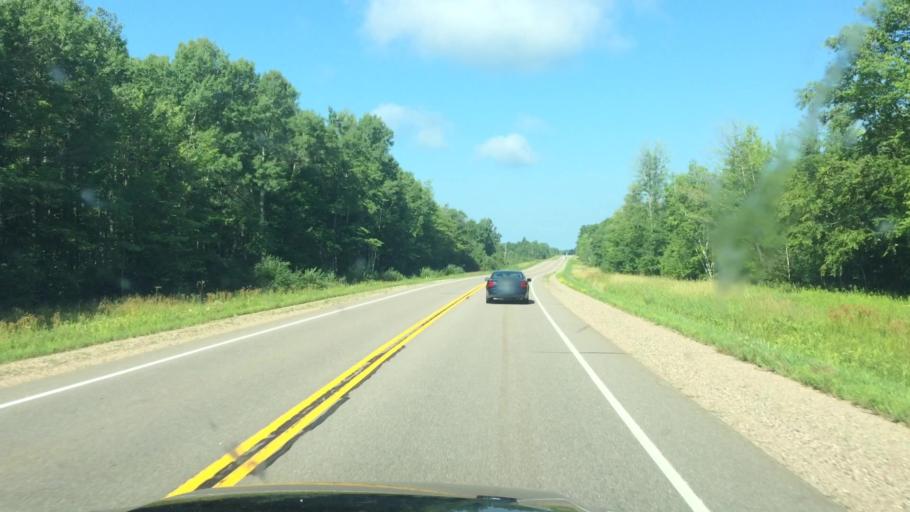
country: US
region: Wisconsin
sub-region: Langlade County
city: Antigo
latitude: 45.1440
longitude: -89.3006
